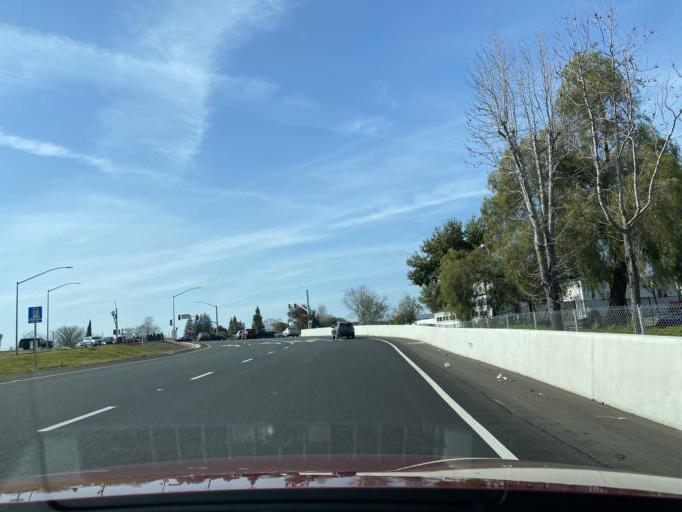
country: US
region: California
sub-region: Sacramento County
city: Rancho Cordova
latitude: 38.5925
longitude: -121.2863
